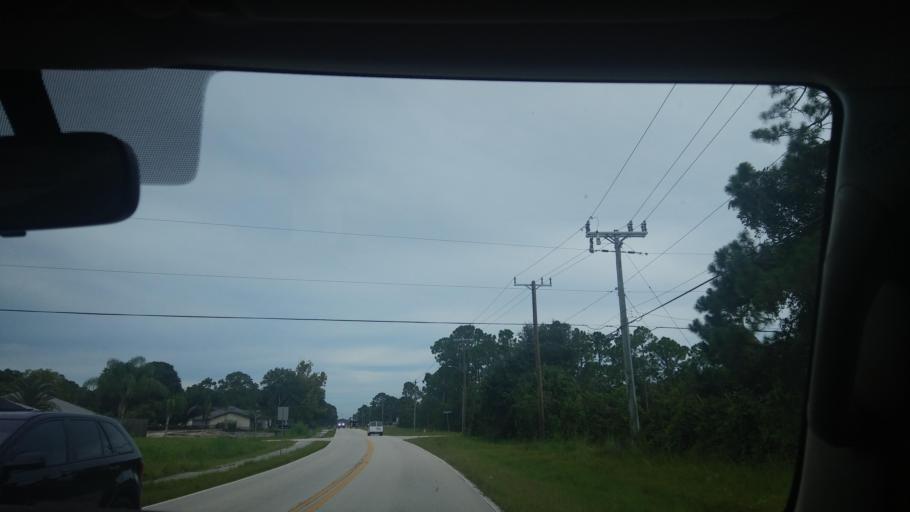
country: US
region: Florida
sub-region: Brevard County
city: Grant-Valkaria
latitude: 27.9614
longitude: -80.6344
